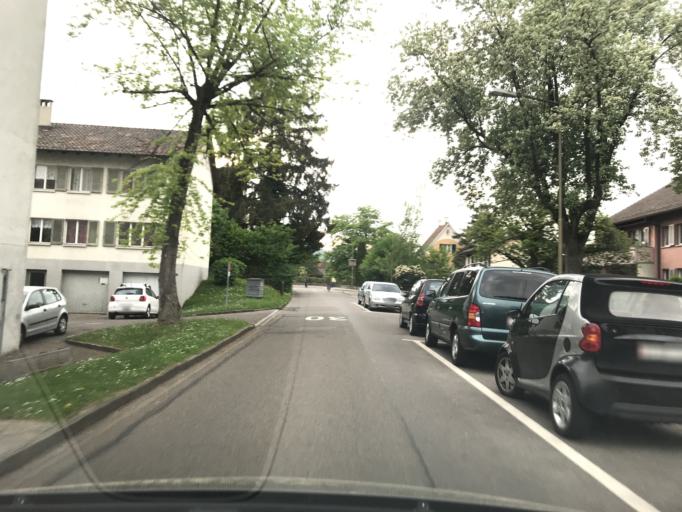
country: CH
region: Zurich
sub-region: Bezirk Winterthur
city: Wuelflingen (Kreis 6) / Lindenplatz
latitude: 47.5073
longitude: 8.6948
